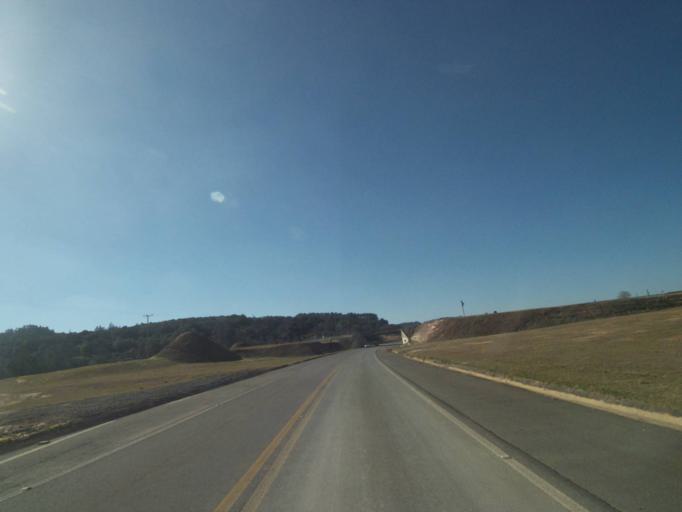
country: BR
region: Parana
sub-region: Tibagi
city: Tibagi
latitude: -24.8169
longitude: -50.4881
